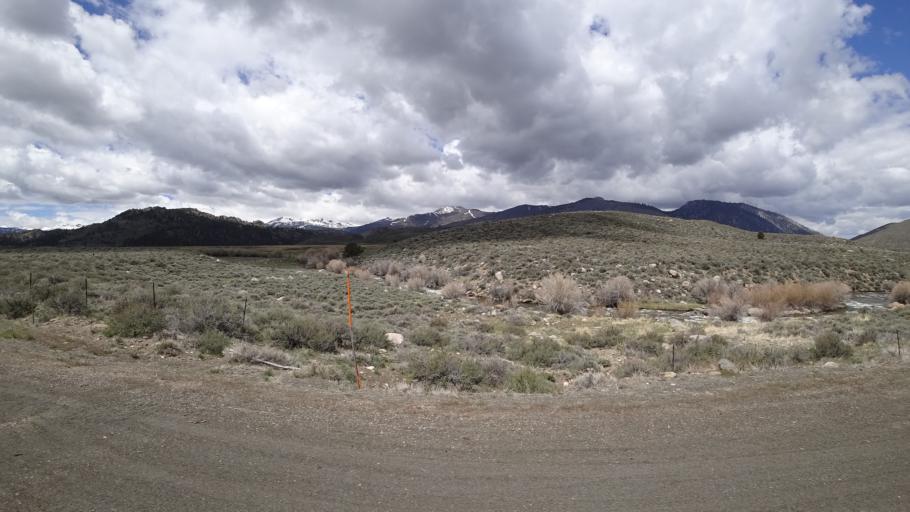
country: US
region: California
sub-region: Mono County
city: Bridgeport
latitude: 38.3568
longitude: -119.4453
